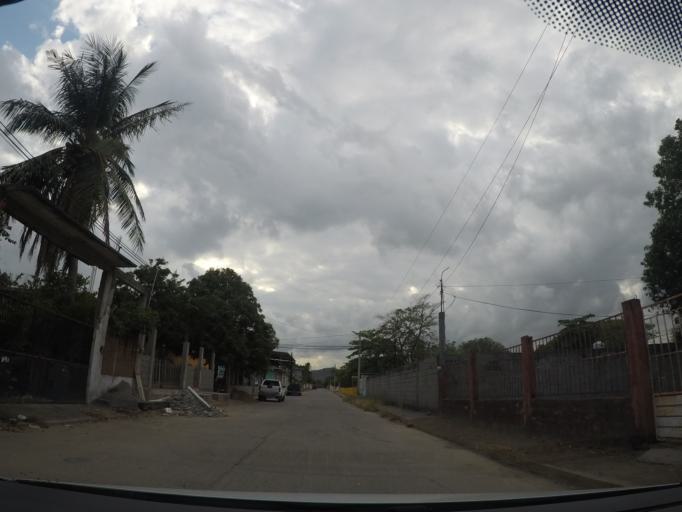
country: MX
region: Oaxaca
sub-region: Salina Cruz
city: Salina Cruz
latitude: 16.2145
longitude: -95.1971
